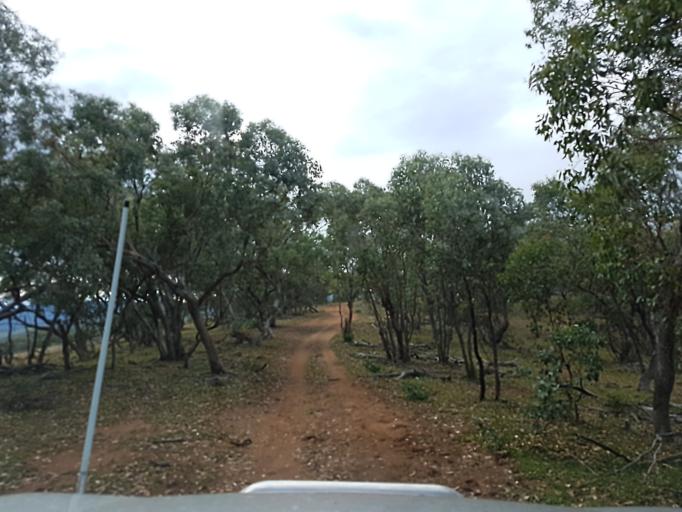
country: AU
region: New South Wales
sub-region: Snowy River
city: Jindabyne
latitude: -36.9688
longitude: 148.3866
